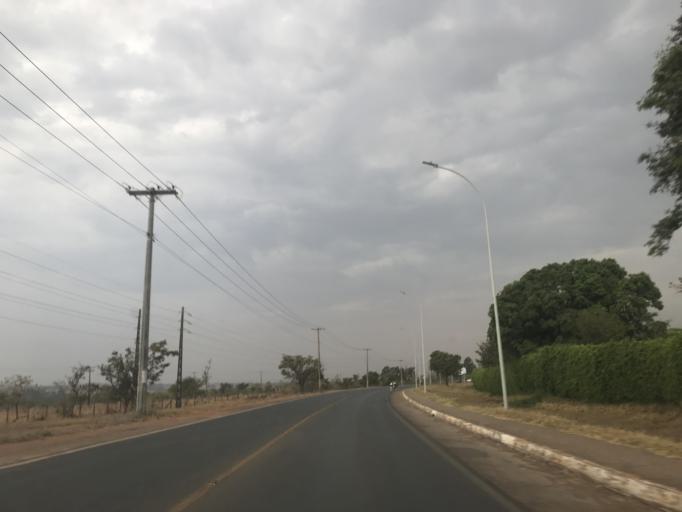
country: BR
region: Federal District
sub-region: Brasilia
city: Brasilia
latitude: -15.6652
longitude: -47.8204
